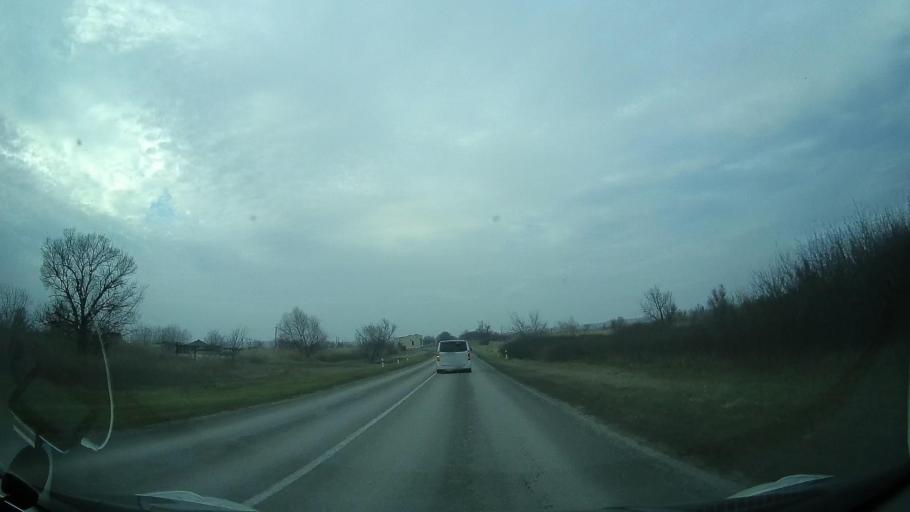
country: RU
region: Rostov
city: Ol'ginskaya
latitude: 47.2115
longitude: 39.9173
